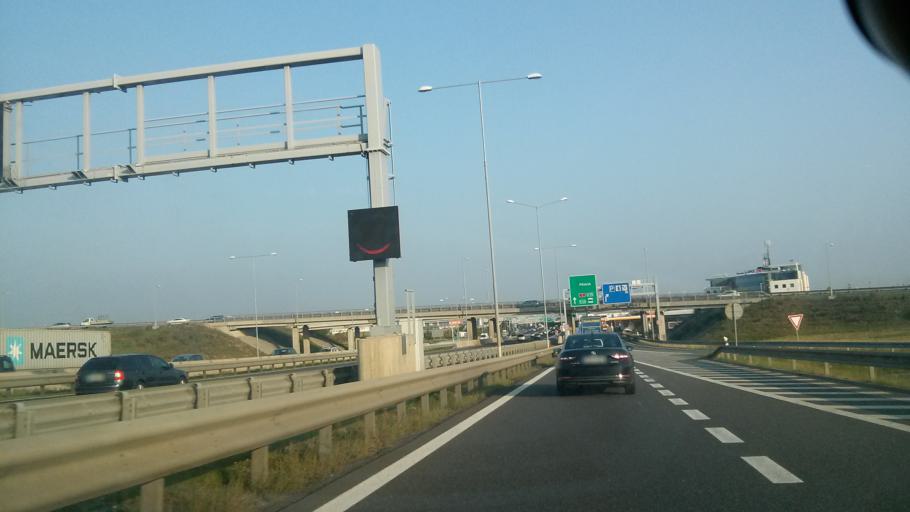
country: CZ
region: Central Bohemia
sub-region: Okres Praha-Vychod
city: Ricany
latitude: 49.9816
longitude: 14.6058
